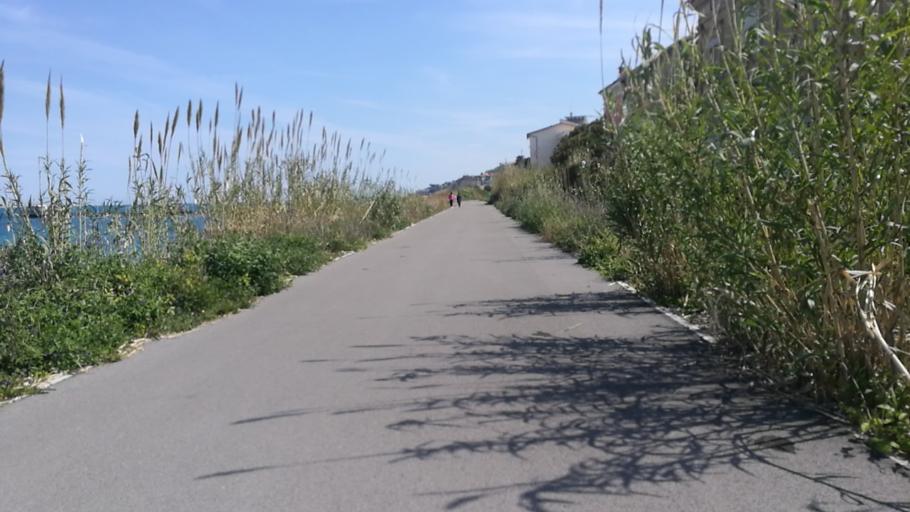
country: IT
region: Abruzzo
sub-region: Provincia di Chieti
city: Marina di San Vito
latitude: 42.3127
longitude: 14.4401
